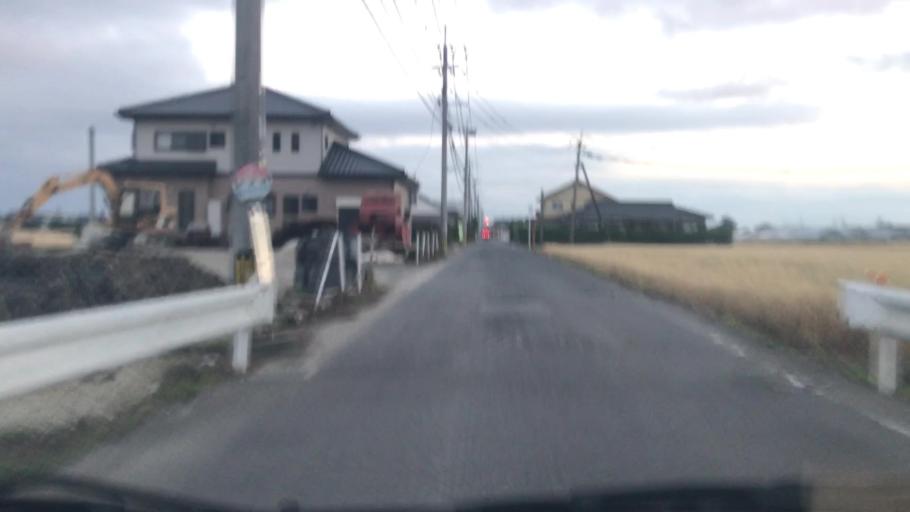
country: JP
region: Saga Prefecture
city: Saga-shi
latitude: 33.2307
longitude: 130.3019
